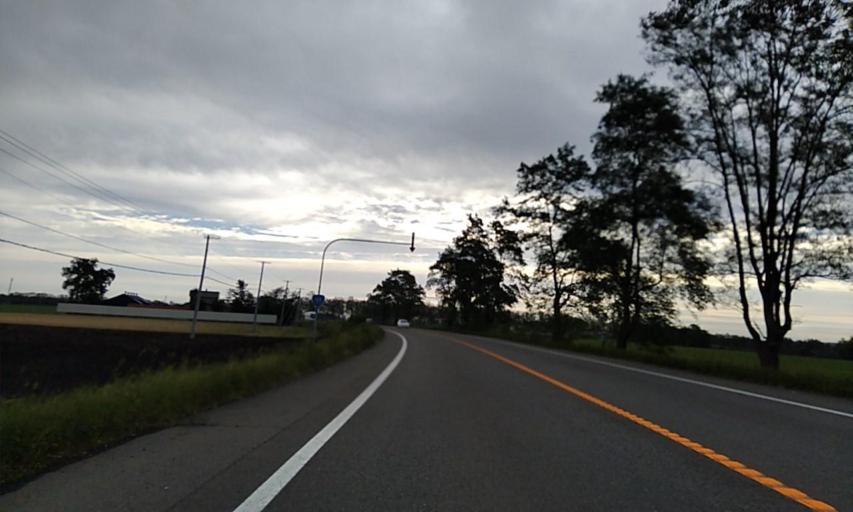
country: JP
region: Hokkaido
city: Obihiro
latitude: 42.9181
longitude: 143.0011
